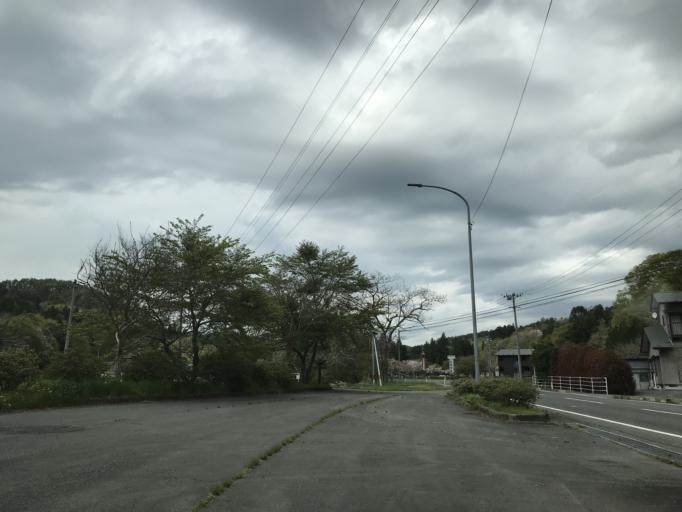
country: JP
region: Iwate
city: Ichinoseki
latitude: 38.7837
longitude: 141.3257
